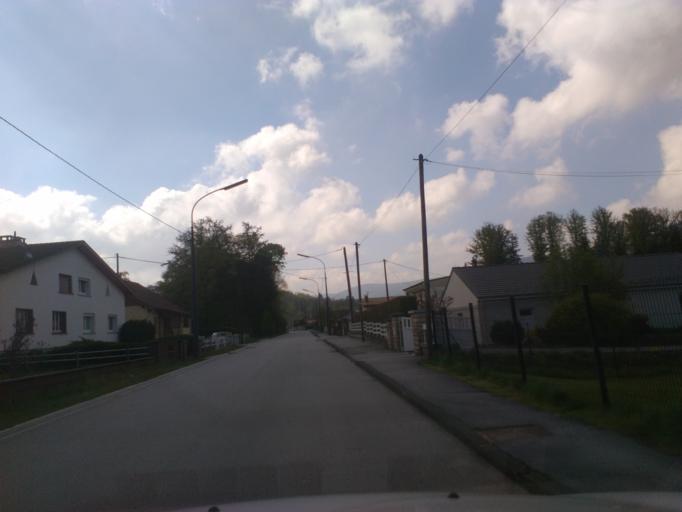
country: FR
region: Lorraine
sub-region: Departement des Vosges
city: Vagney
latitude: 48.0037
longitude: 6.7196
